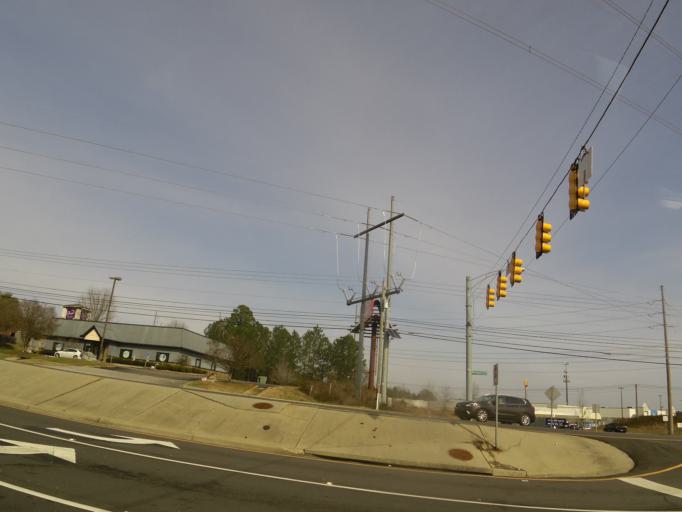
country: US
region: Alabama
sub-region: Houston County
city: Dothan
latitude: 31.2668
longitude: -85.4438
